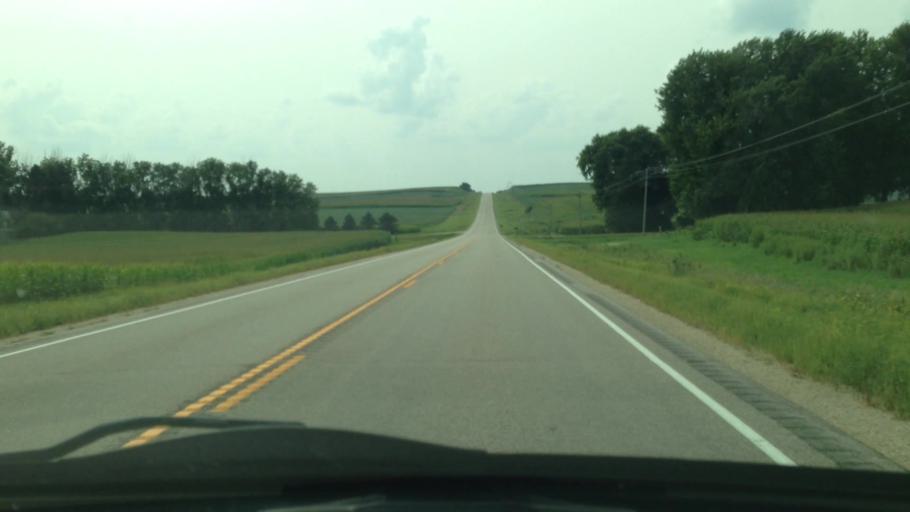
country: US
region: Minnesota
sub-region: Wabasha County
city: Elgin
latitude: 44.1653
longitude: -92.2281
